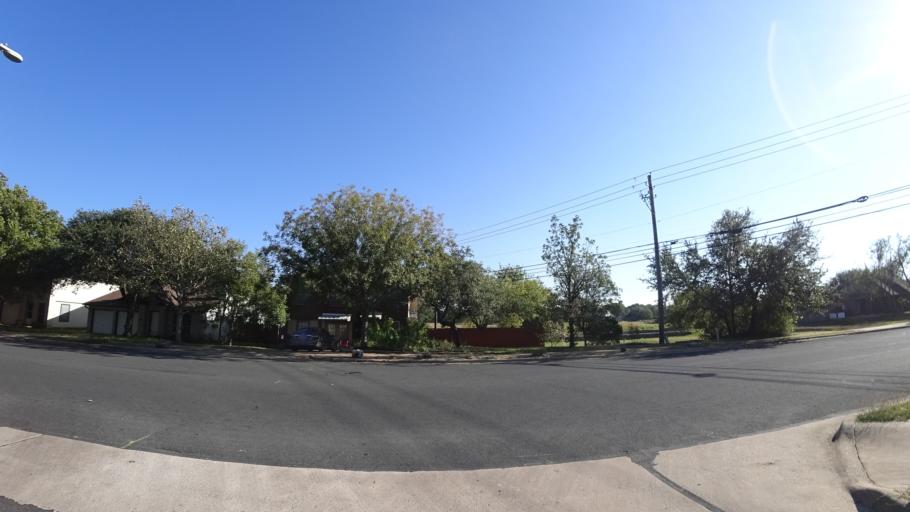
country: US
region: Texas
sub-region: Travis County
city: Shady Hollow
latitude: 30.2055
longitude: -97.8528
